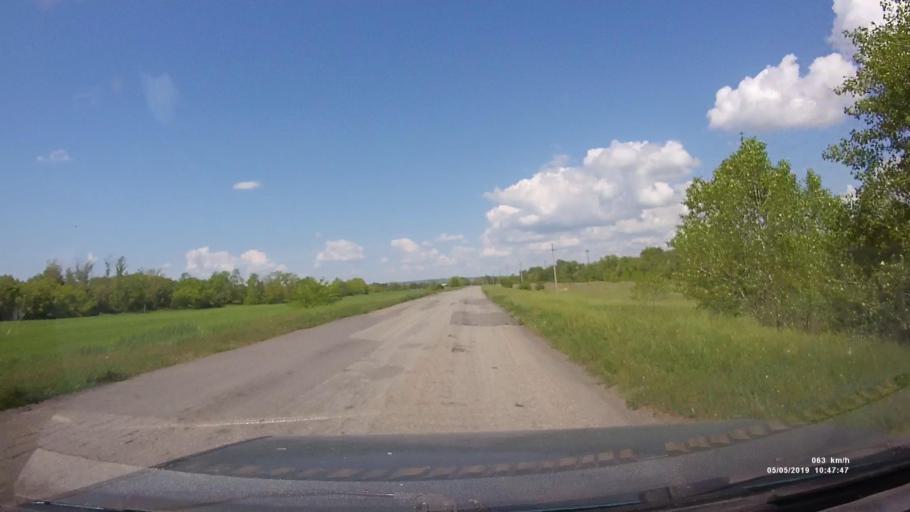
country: RU
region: Rostov
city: Ust'-Donetskiy
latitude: 47.6398
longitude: 40.8282
